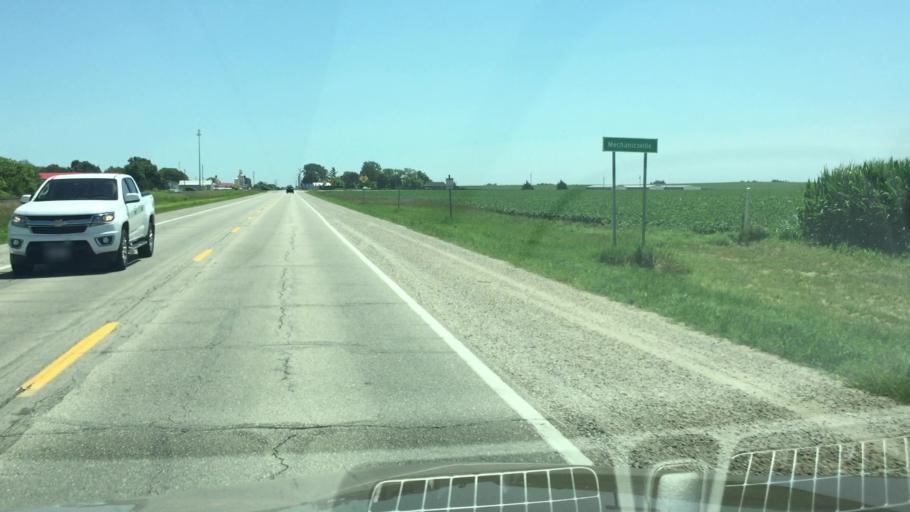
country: US
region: Iowa
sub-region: Cedar County
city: Mechanicsville
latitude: 41.9043
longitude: -91.2642
